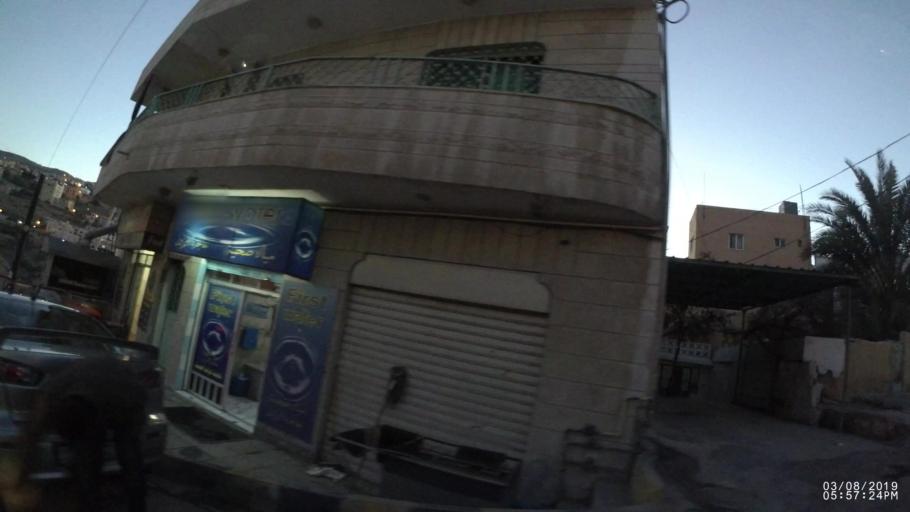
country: JO
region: Ma'an
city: Petra
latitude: 30.3236
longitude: 35.4772
